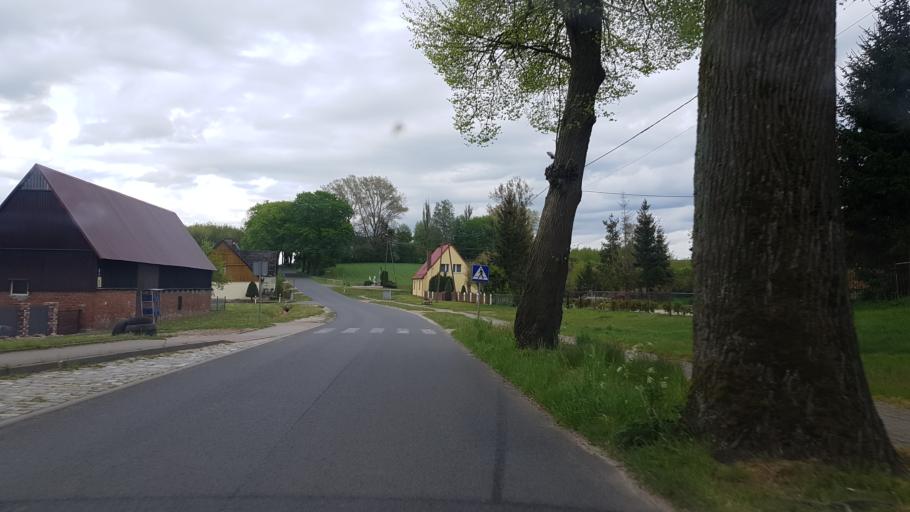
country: PL
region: West Pomeranian Voivodeship
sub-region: Powiat slawienski
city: Slawno
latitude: 54.2727
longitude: 16.5296
